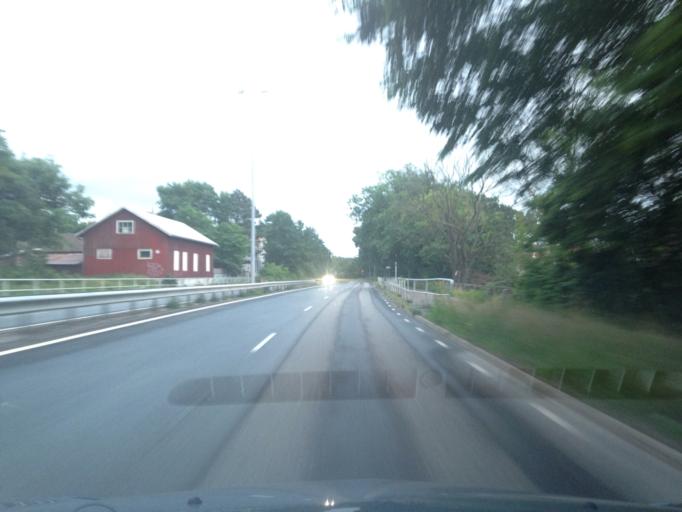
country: SE
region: Halland
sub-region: Varbergs Kommun
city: Varberg
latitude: 57.1145
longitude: 12.2604
